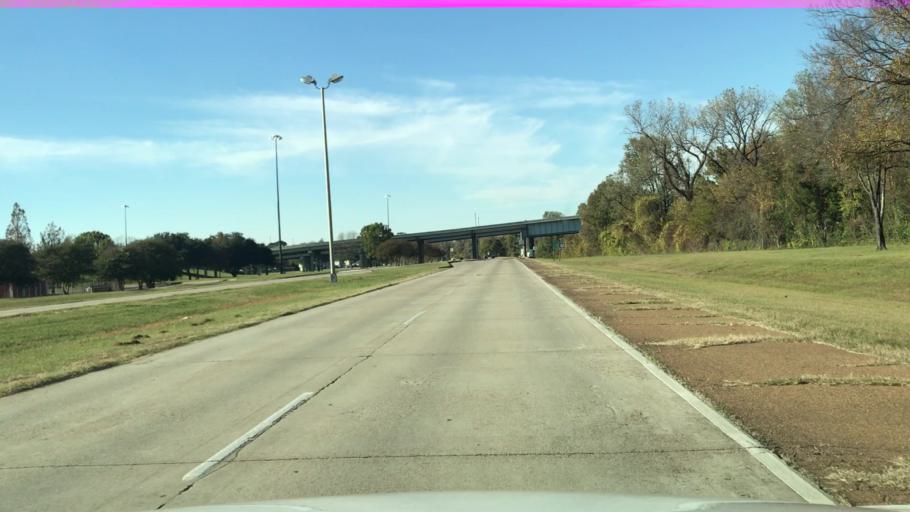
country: US
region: Louisiana
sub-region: Bossier Parish
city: Bossier City
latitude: 32.4888
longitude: -93.6986
